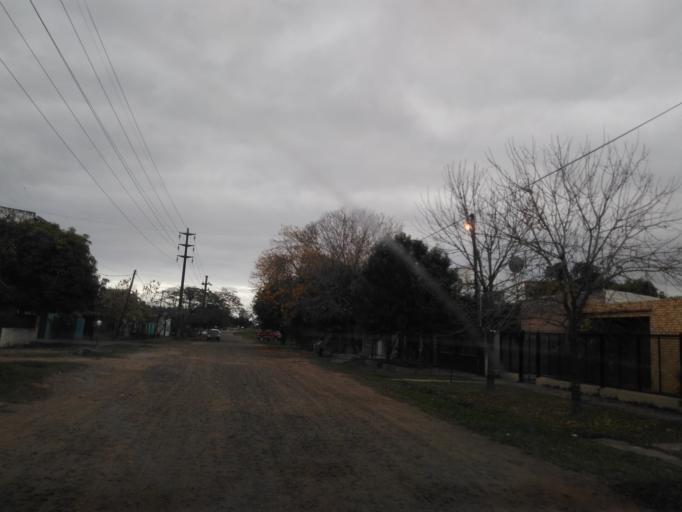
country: AR
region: Chaco
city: Fontana
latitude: -27.4043
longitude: -58.9972
